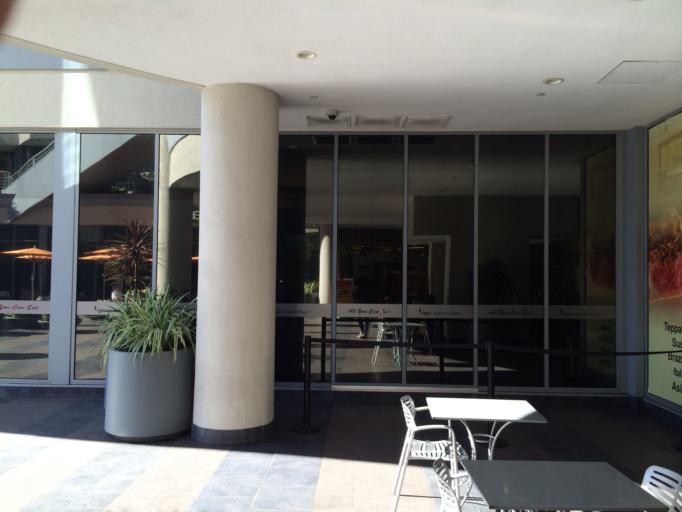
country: US
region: California
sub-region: Los Angeles County
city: Hollywood
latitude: 34.1019
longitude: -118.3428
